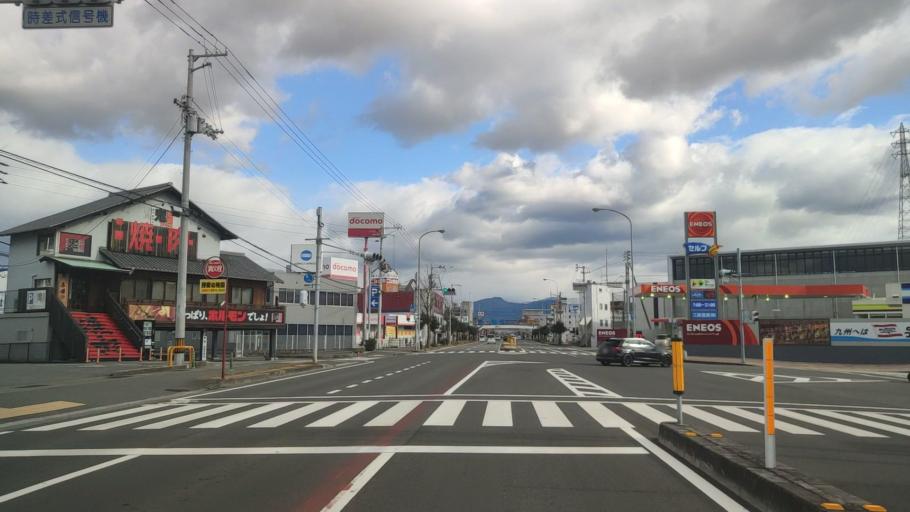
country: JP
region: Ehime
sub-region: Shikoku-chuo Shi
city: Matsuyama
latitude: 33.8143
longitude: 132.7403
